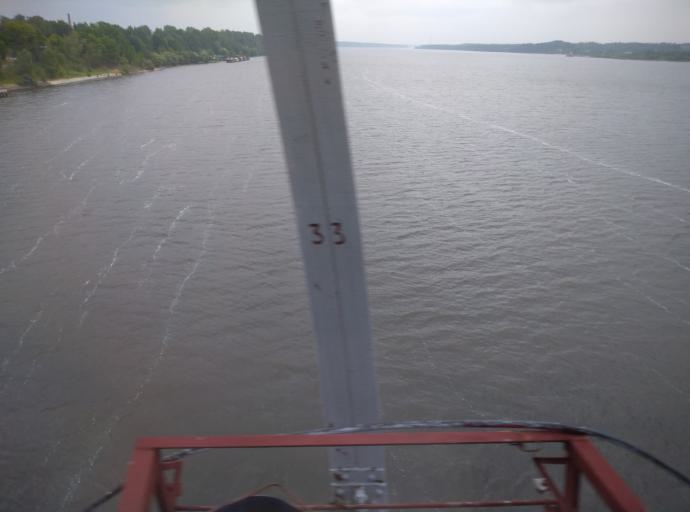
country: RU
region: Kostroma
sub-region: Kostromskoy Rayon
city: Kostroma
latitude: 57.7398
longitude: 40.9580
